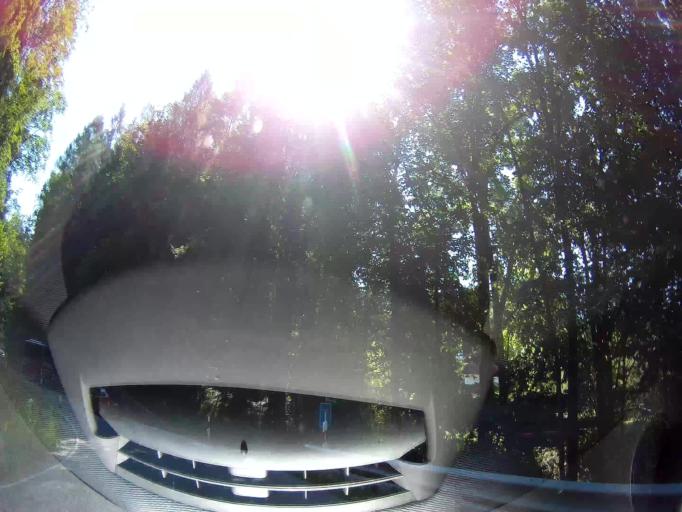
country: DE
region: Bavaria
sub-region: Upper Bavaria
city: Marktschellenberg
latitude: 47.6520
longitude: 13.0499
